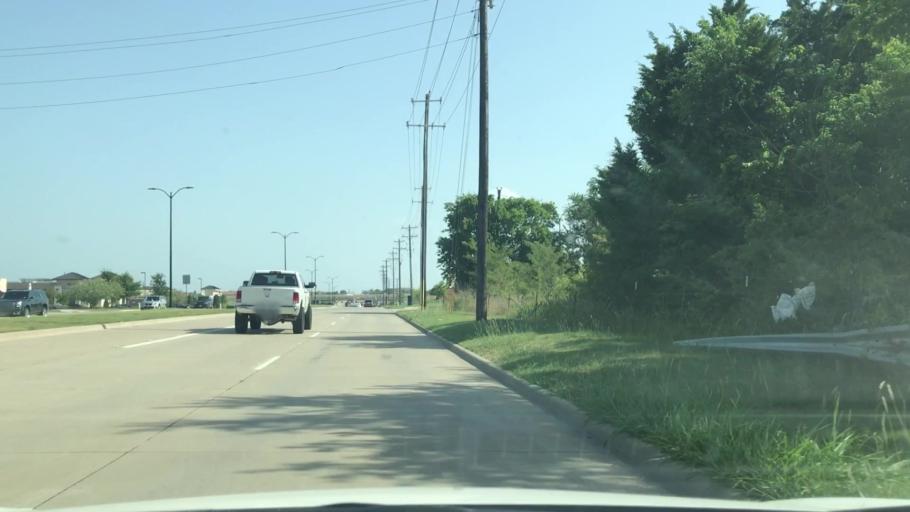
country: US
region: Texas
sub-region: Collin County
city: Frisco
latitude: 33.1237
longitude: -96.7509
